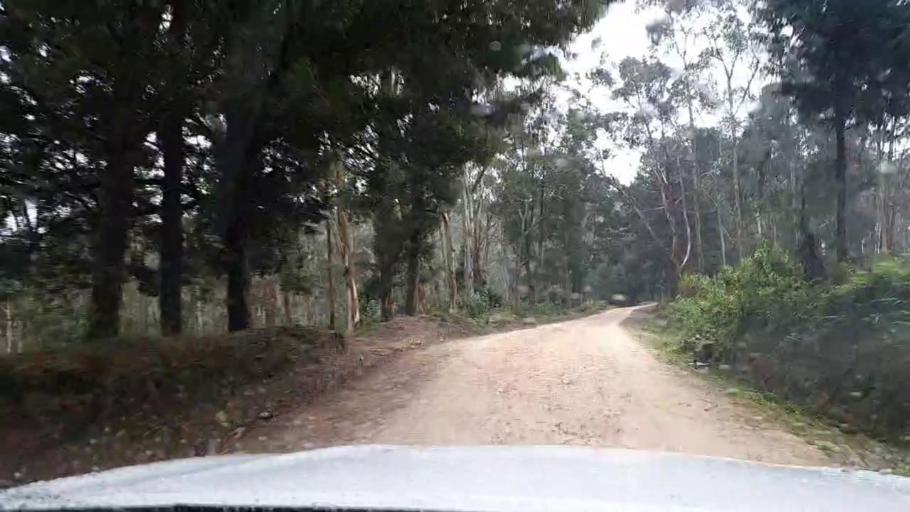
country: RW
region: Southern Province
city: Nzega
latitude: -2.3640
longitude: 29.3796
